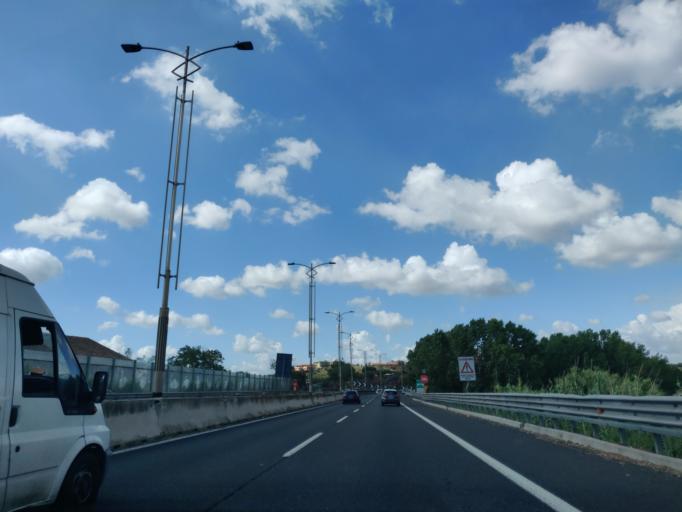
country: IT
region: Latium
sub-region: Citta metropolitana di Roma Capitale
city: Vitinia
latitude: 41.8278
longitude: 12.4200
